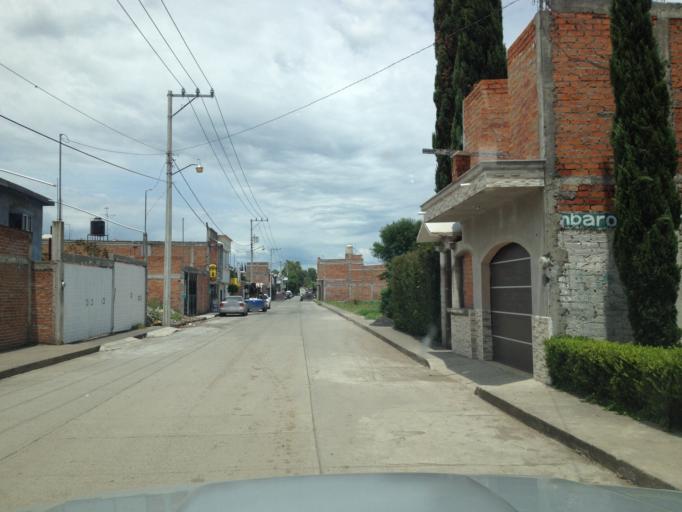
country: MX
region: Michoacan
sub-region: Tarimbaro
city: El Colegio
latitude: 19.7913
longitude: -101.1773
